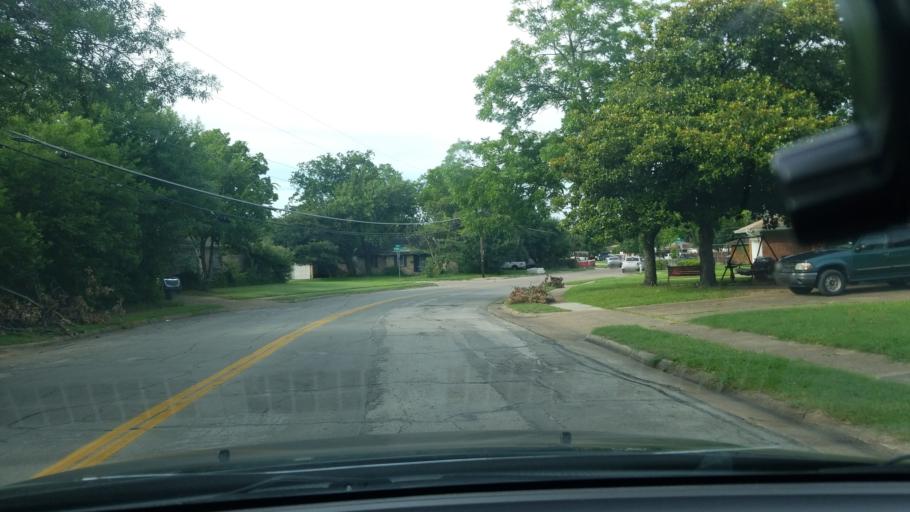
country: US
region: Texas
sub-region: Dallas County
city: Balch Springs
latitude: 32.7544
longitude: -96.6736
